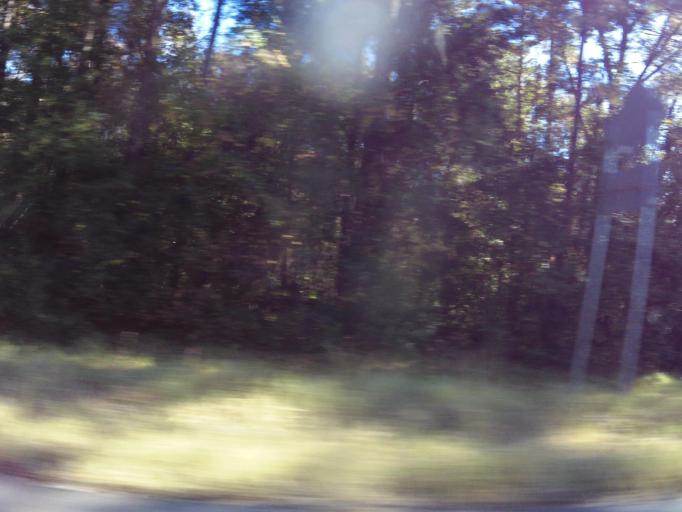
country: US
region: Georgia
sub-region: Liberty County
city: Midway
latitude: 31.8590
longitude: -81.4004
